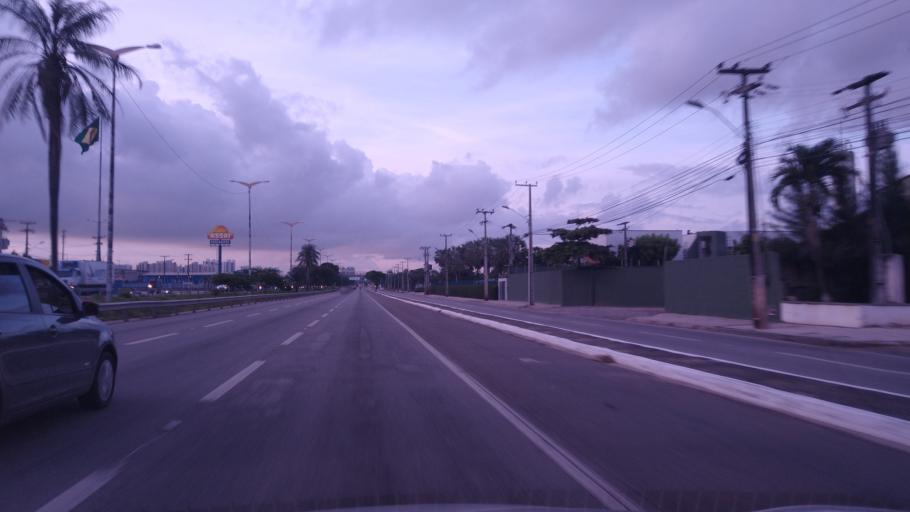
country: BR
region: Ceara
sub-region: Fortaleza
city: Fortaleza
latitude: -3.7902
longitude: -38.5099
